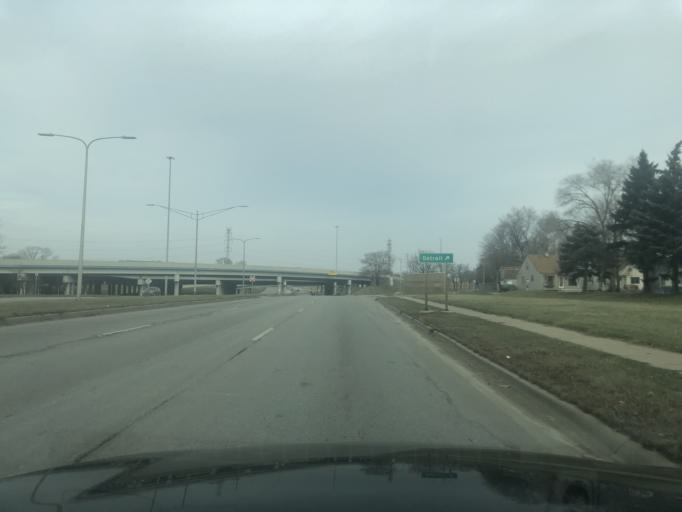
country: US
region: Michigan
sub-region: Wayne County
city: Lincoln Park
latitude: 42.2410
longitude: -83.1949
